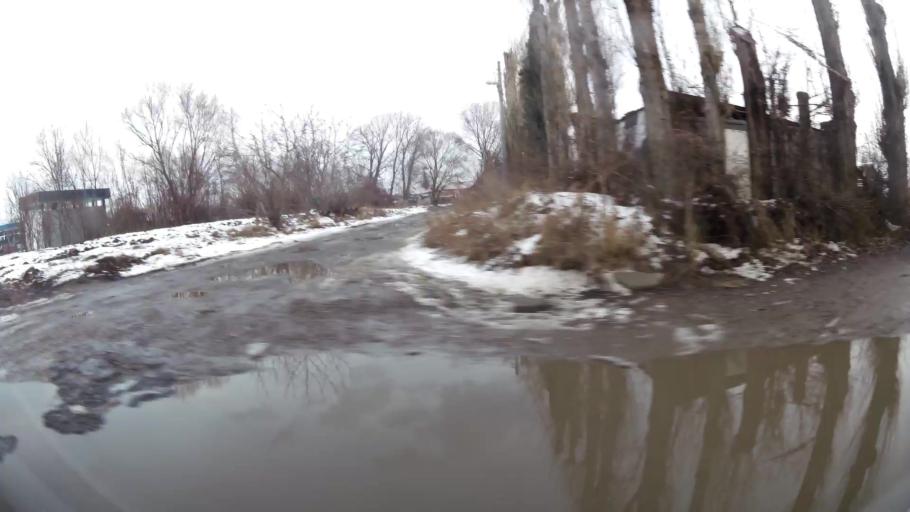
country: BG
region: Sofia-Capital
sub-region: Stolichna Obshtina
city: Sofia
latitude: 42.7303
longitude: 23.3441
